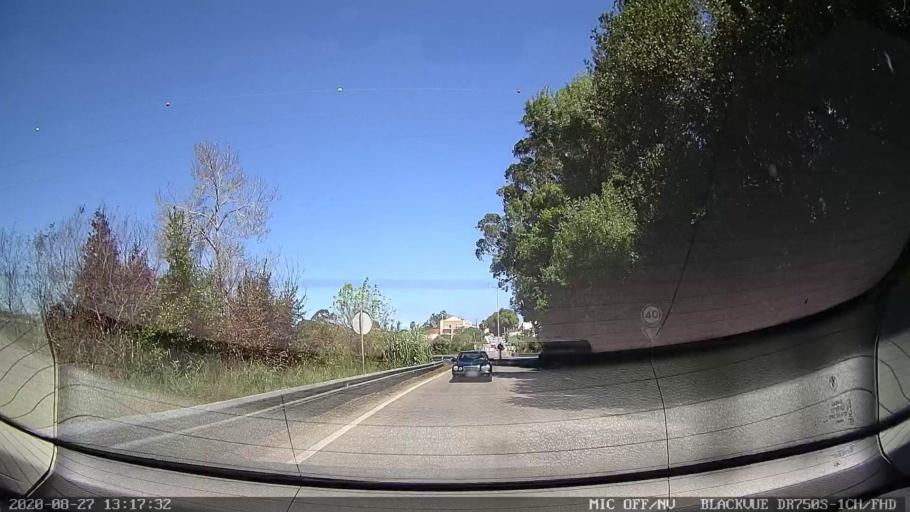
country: PT
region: Aveiro
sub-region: Ilhavo
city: Ilhavo
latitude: 40.5810
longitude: -8.6809
